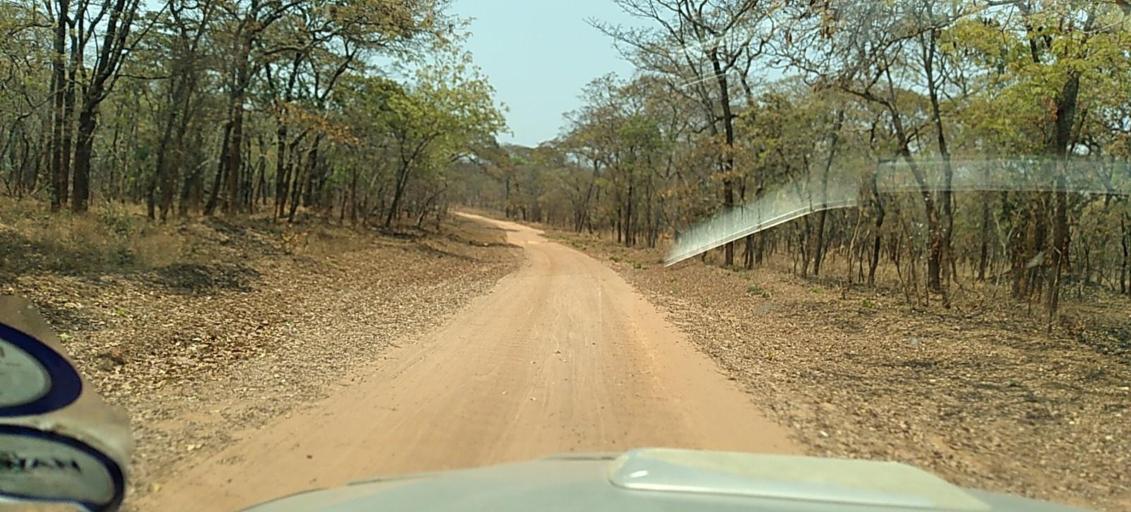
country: ZM
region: North-Western
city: Kasempa
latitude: -13.5519
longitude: 26.0642
